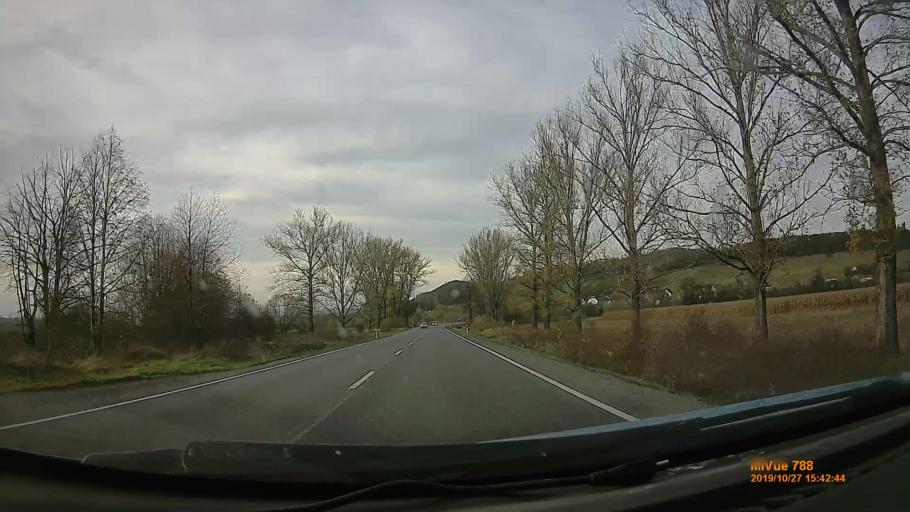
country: PL
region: Lower Silesian Voivodeship
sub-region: Powiat klodzki
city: Klodzko
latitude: 50.4625
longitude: 16.6247
